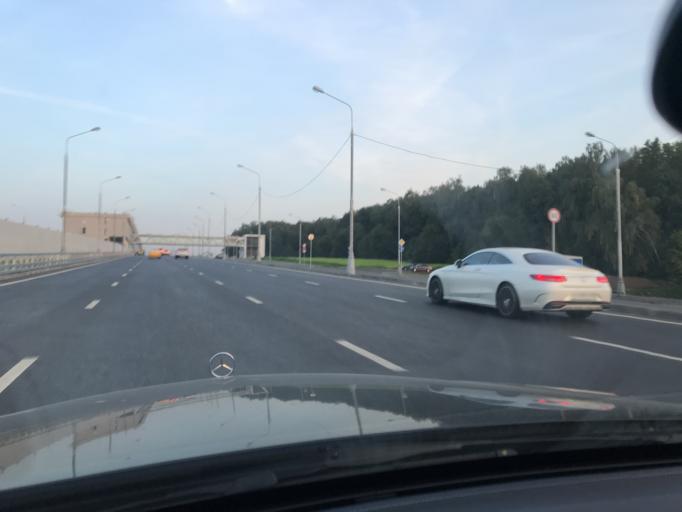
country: RU
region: Moskovskaya
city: Mosrentgen
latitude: 55.5878
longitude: 37.4291
